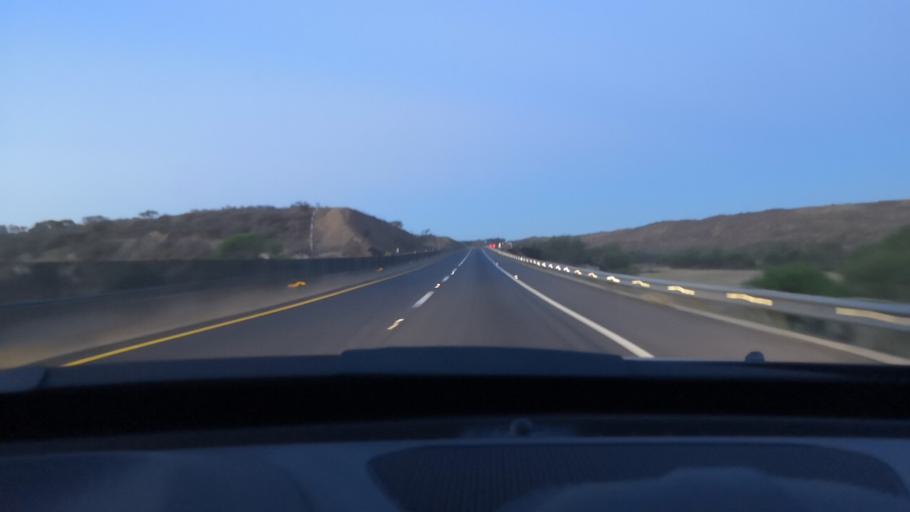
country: MX
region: Jalisco
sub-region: San Juan de los Lagos
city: Mezquitic de la Magdalena
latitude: 21.1906
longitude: -102.3510
